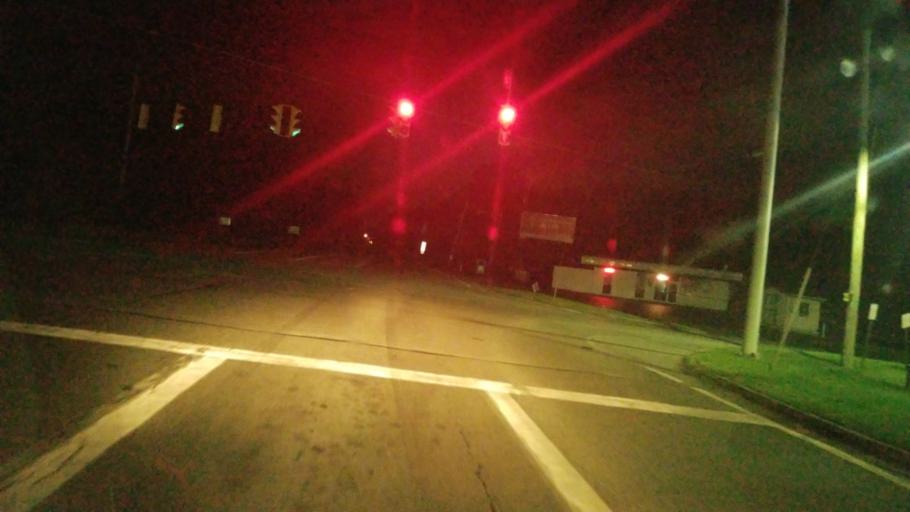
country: US
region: Ohio
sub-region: Trumbull County
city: McDonald
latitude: 41.1435
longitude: -80.7224
